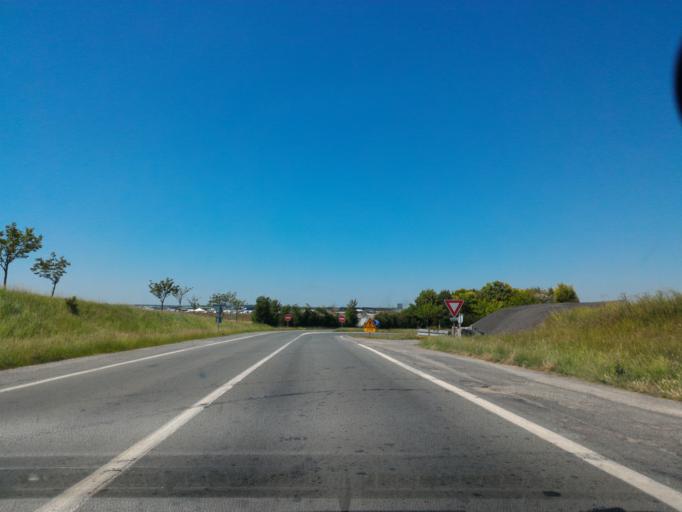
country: FR
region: Poitou-Charentes
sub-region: Departement de la Vienne
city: Migne-Auxances
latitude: 46.6190
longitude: 0.3396
